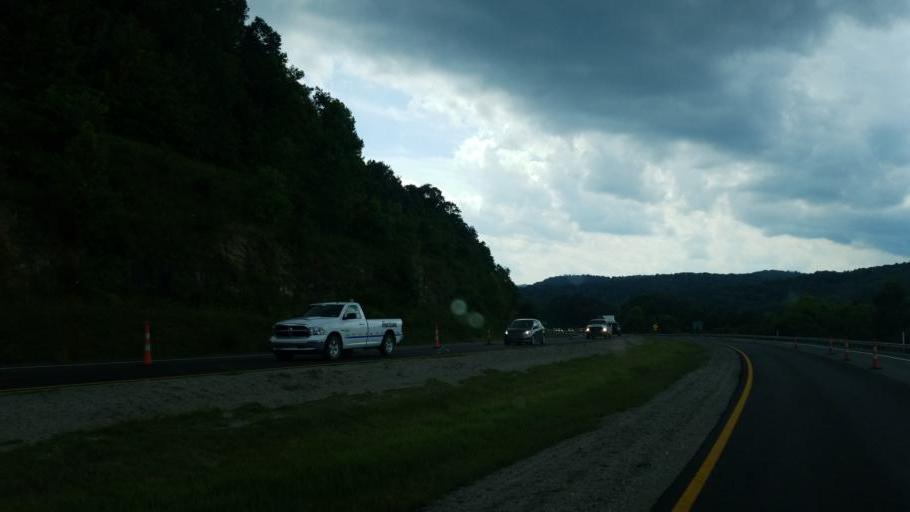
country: US
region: West Virginia
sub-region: Kanawha County
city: Alum Creek
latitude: 38.2682
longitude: -81.8239
